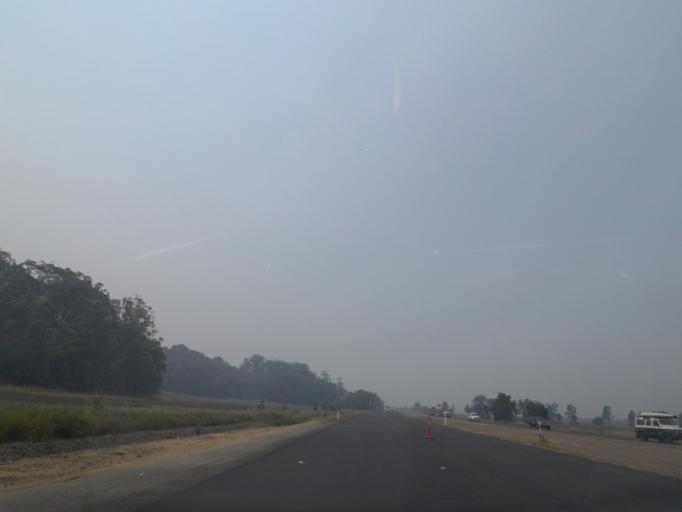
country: AU
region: New South Wales
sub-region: Ballina
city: Ballina
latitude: -28.8835
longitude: 153.4843
